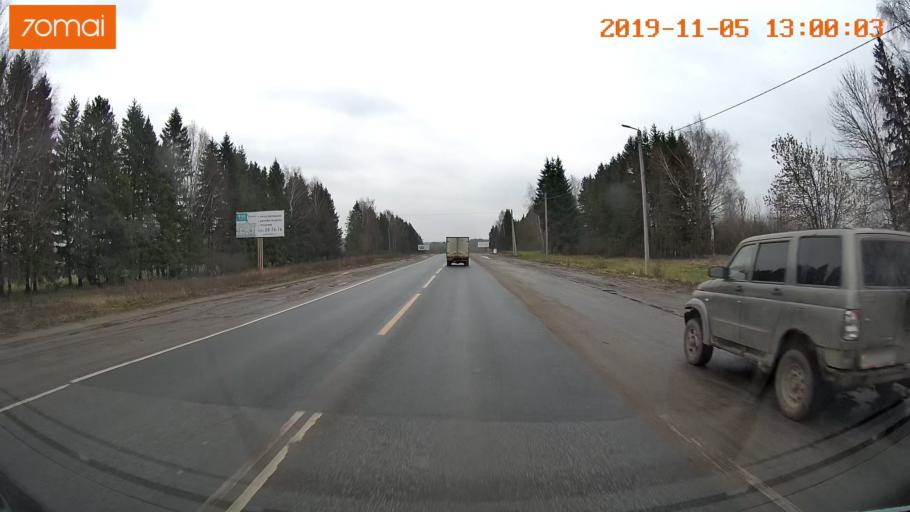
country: RU
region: Ivanovo
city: Kokhma
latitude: 56.9154
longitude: 41.1396
